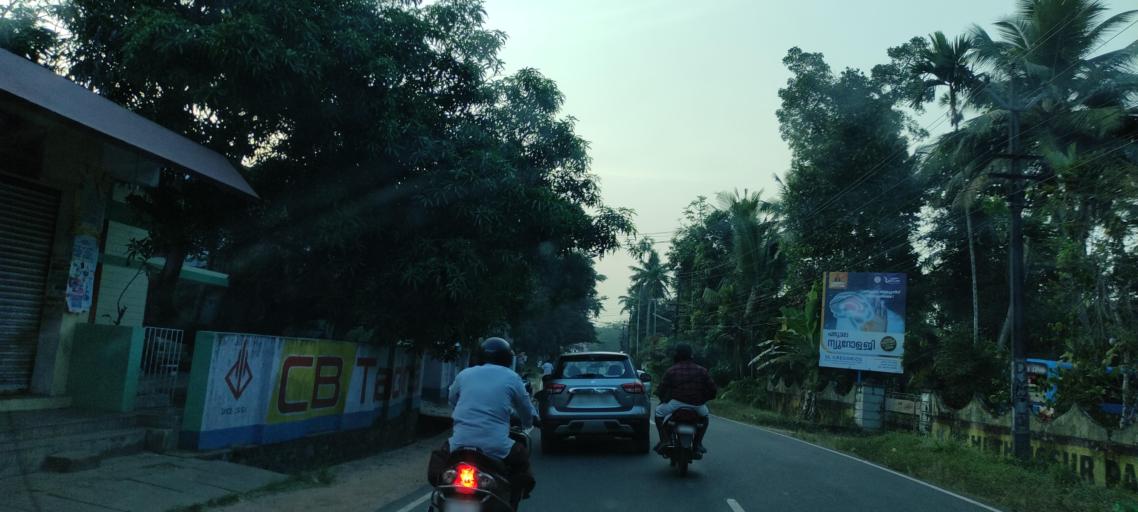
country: IN
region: Kerala
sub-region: Alappuzha
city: Mavelikara
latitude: 9.2781
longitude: 76.5354
